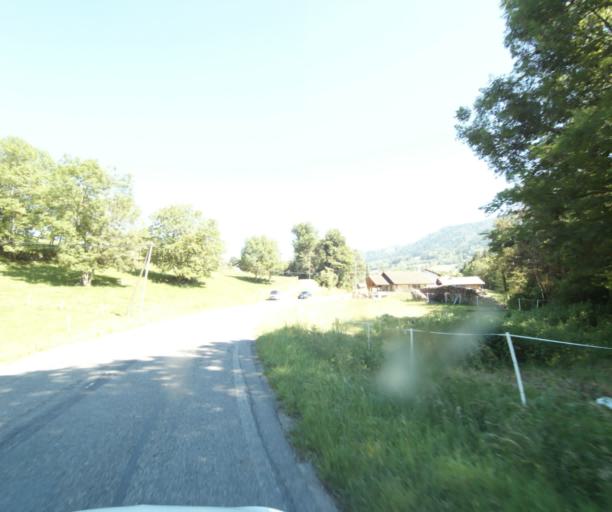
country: FR
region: Rhone-Alpes
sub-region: Departement de la Haute-Savoie
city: Bons-en-Chablais
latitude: 46.2648
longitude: 6.3512
